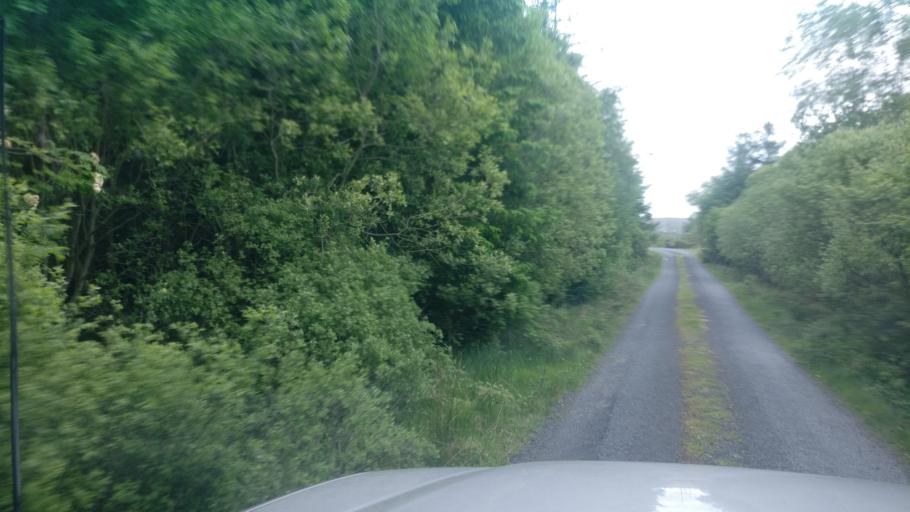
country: IE
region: Connaught
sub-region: County Galway
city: Loughrea
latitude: 53.1129
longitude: -8.6736
